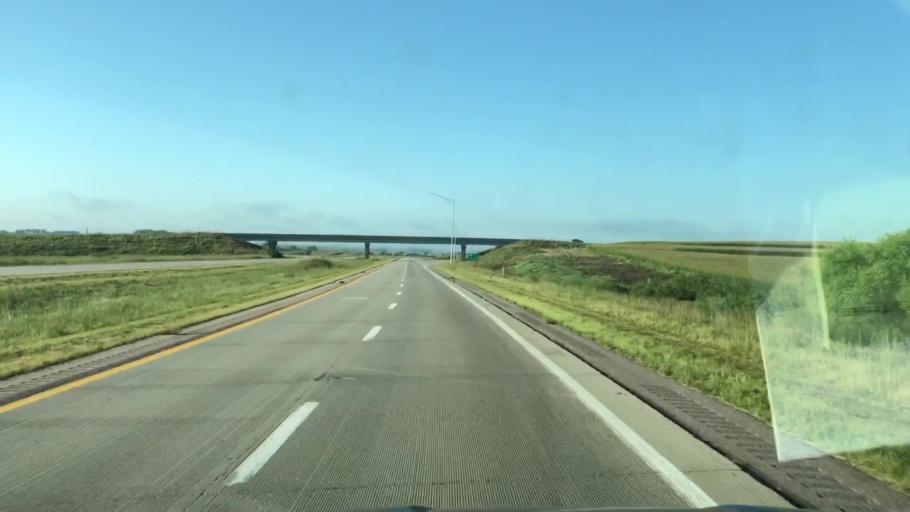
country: US
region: Iowa
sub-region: Sioux County
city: Alton
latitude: 42.9704
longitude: -96.0229
